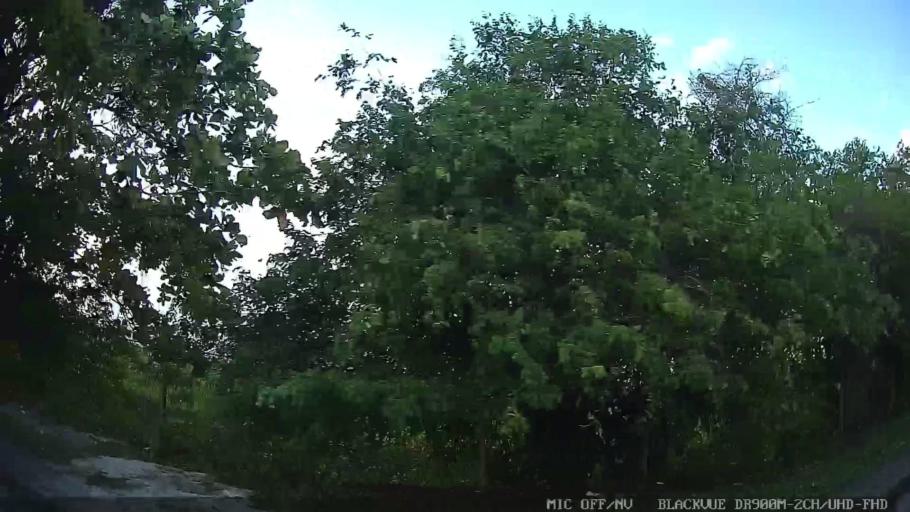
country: BR
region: Sao Paulo
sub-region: Caraguatatuba
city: Caraguatatuba
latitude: -23.6588
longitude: -45.4355
